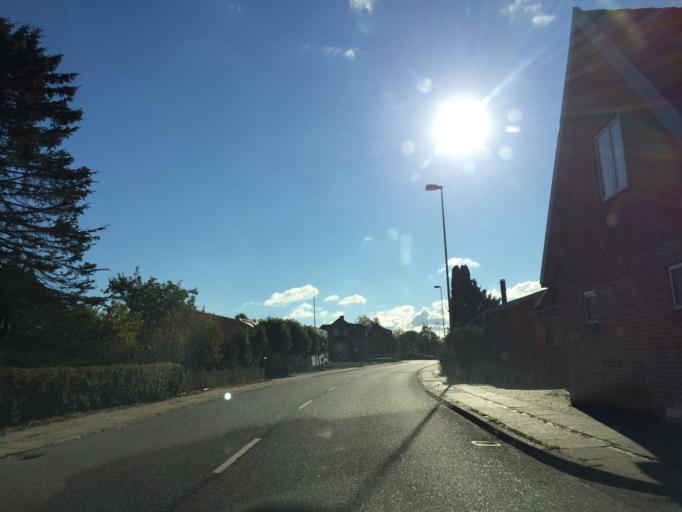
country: DK
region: Central Jutland
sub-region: Randers Kommune
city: Langa
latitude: 56.3582
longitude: 9.9141
